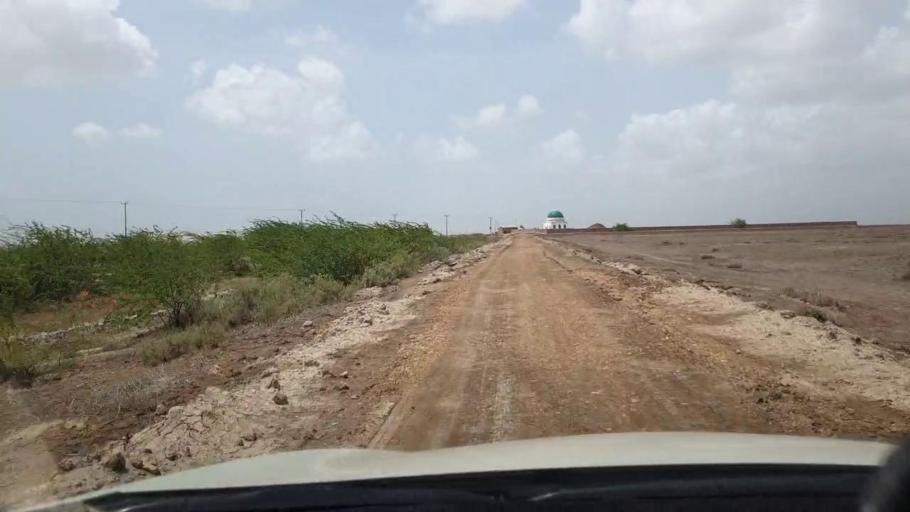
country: PK
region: Sindh
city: Kadhan
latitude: 24.3627
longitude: 68.8476
